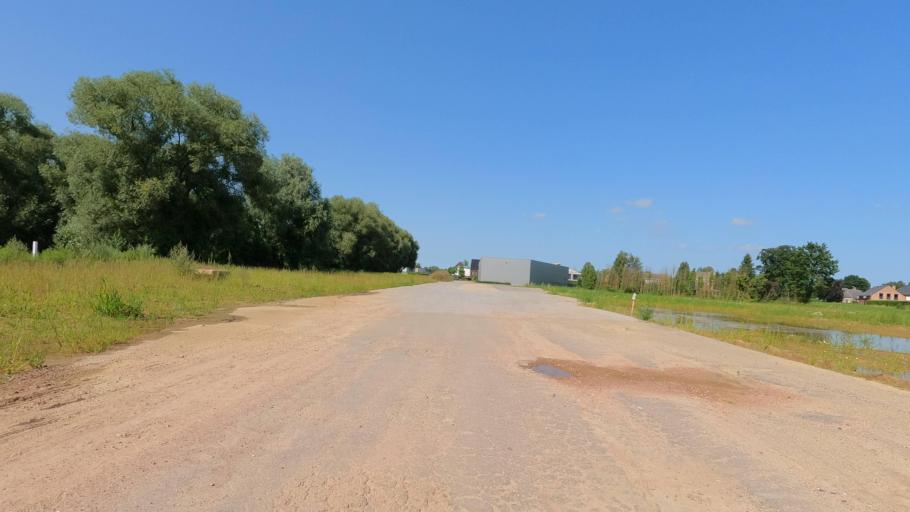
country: BE
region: Flanders
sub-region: Provincie Antwerpen
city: Willebroek
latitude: 51.0366
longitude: 4.3479
